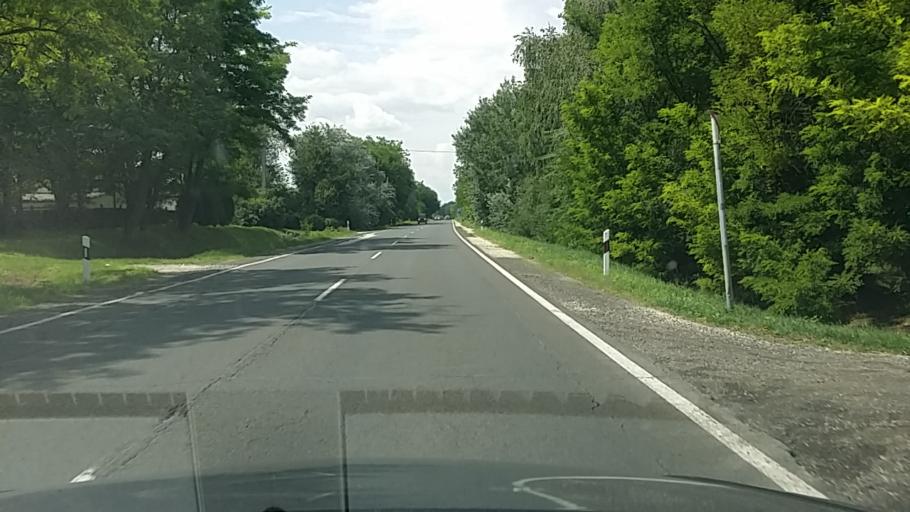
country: HU
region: Bacs-Kiskun
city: Lajosmizse
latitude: 47.0499
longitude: 19.5237
